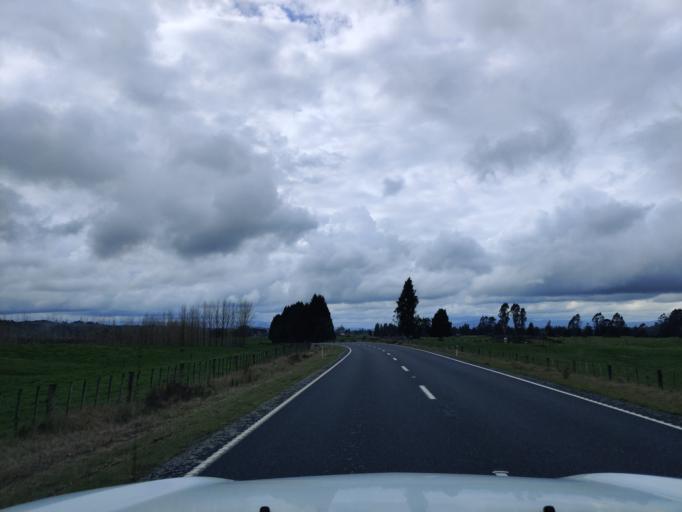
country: NZ
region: Waikato
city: Turangi
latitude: -39.0363
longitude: 175.3830
